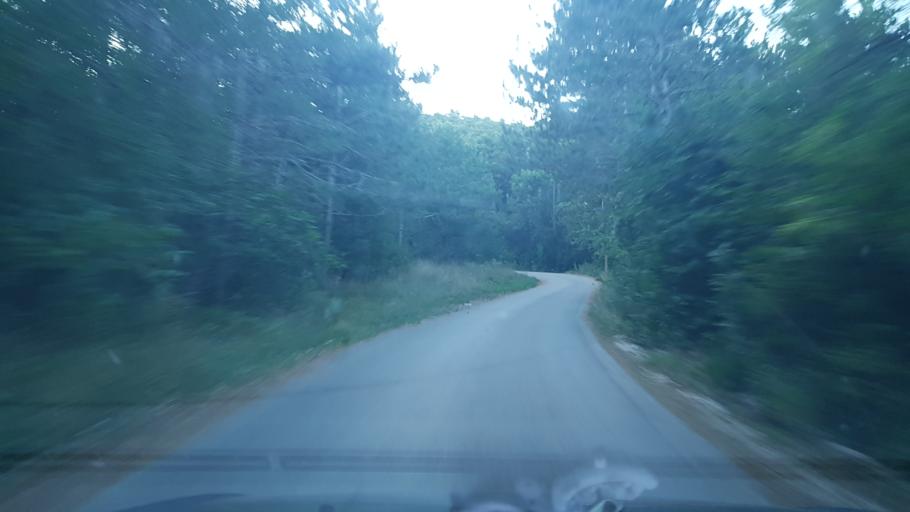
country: SI
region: Vipava
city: Vipava
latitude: 45.7969
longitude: 14.0103
